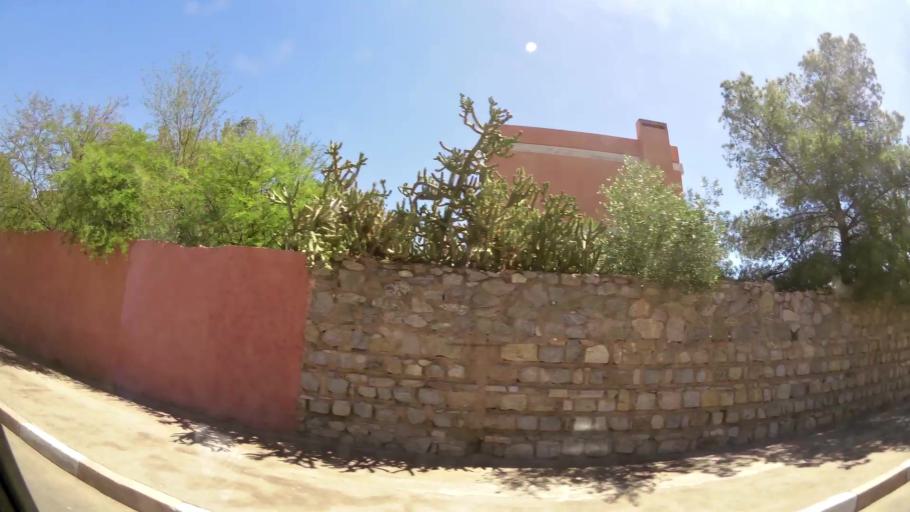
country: MA
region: Marrakech-Tensift-Al Haouz
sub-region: Marrakech
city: Marrakesh
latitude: 31.6483
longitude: -7.9906
